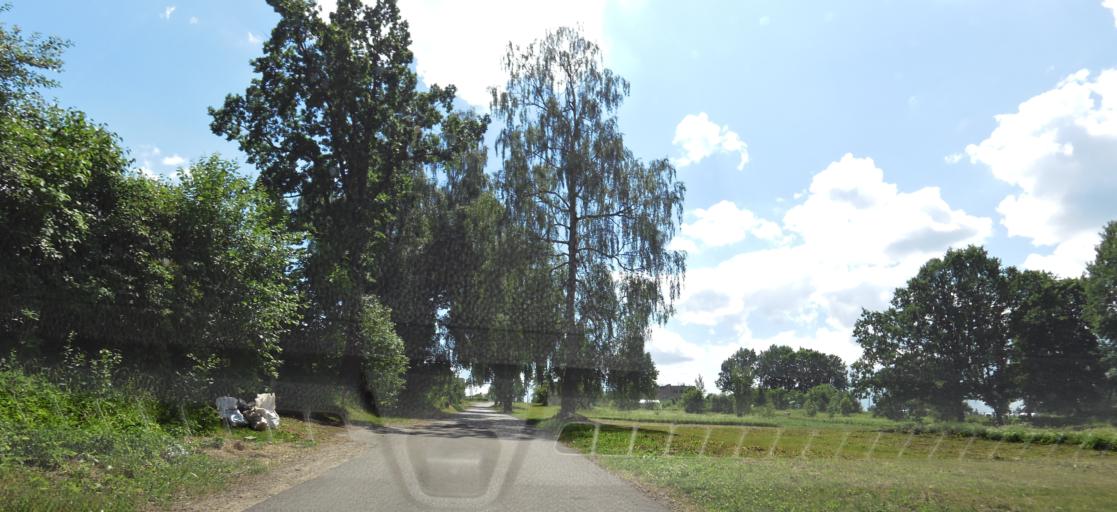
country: LT
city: Skaidiskes
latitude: 54.5388
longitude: 25.6521
